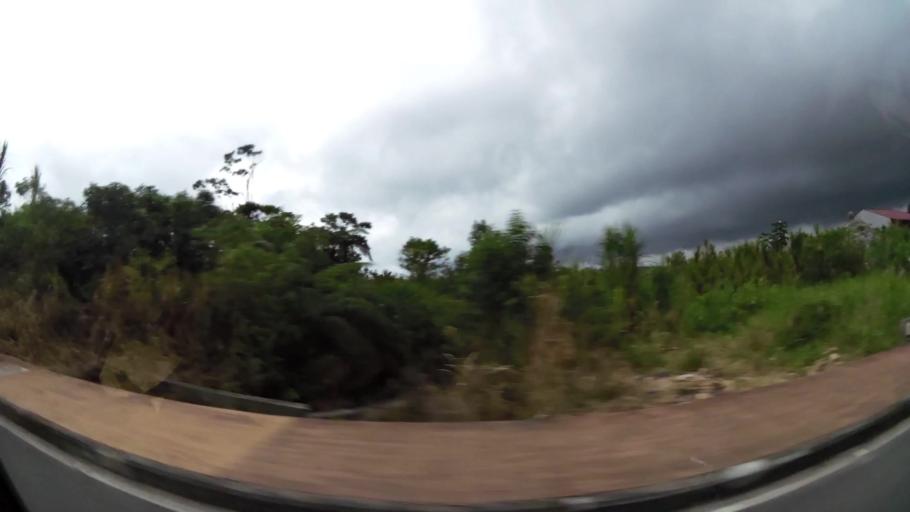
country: EC
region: Pastaza
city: Puyo
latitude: -1.4822
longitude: -78.0074
